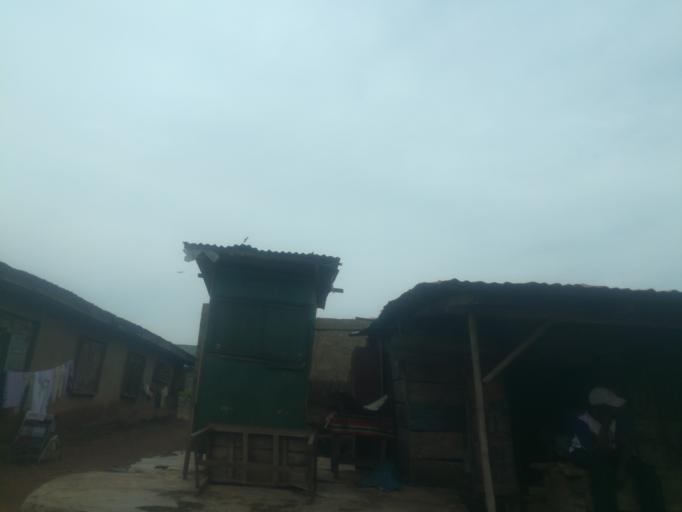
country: NG
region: Oyo
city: Ibadan
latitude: 7.3733
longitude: 3.9319
